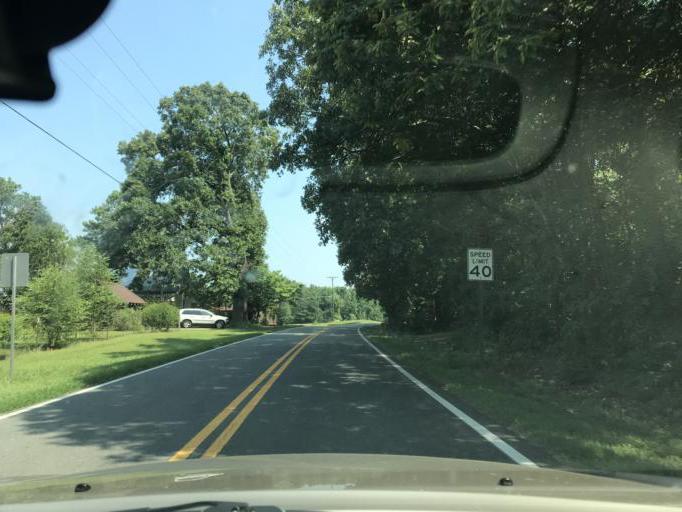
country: US
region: Georgia
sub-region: Hall County
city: Flowery Branch
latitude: 34.2360
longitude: -83.9975
